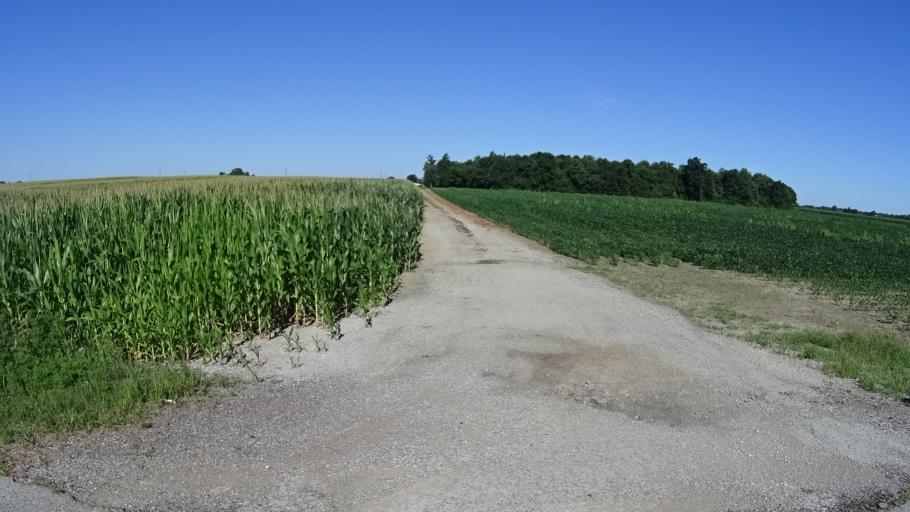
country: US
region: Ohio
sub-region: Erie County
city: Sandusky
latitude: 41.3858
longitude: -82.7223
